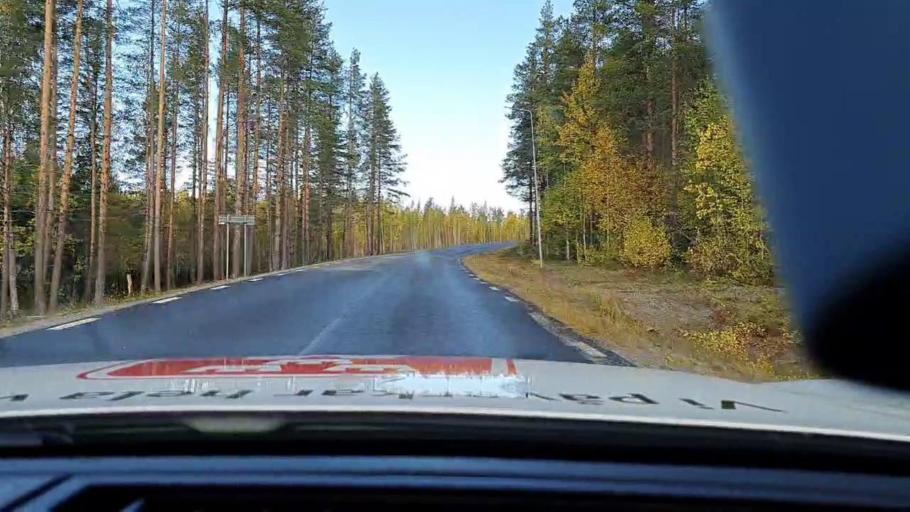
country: SE
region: Vaesterbotten
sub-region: Skelleftea Kommun
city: Langsele
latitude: 64.9485
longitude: 20.0222
